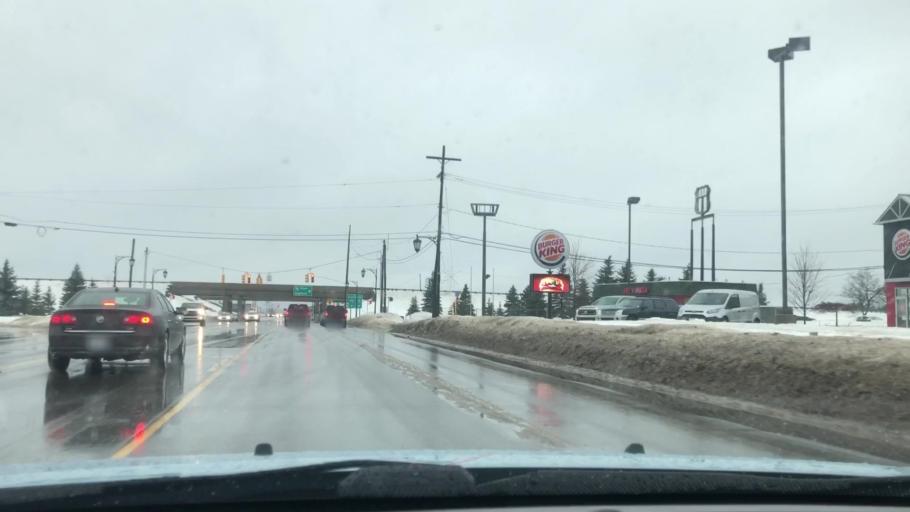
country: US
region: Michigan
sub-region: Otsego County
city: Gaylord
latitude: 45.0274
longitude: -84.6854
